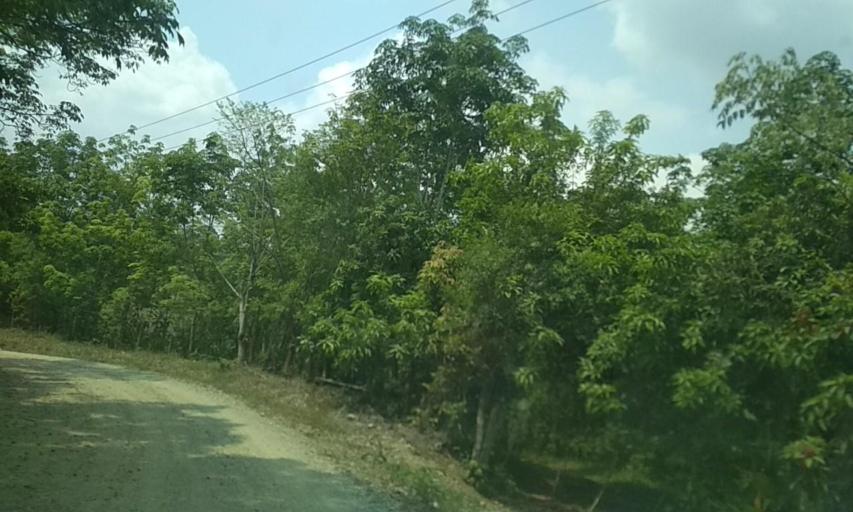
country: MX
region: Tabasco
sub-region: Huimanguillo
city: Francisco Rueda
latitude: 17.6346
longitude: -93.8221
